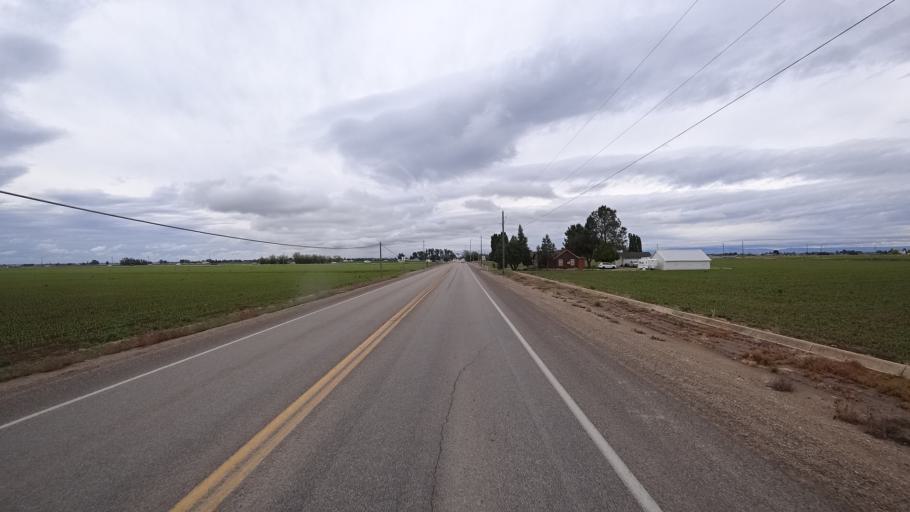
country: US
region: Idaho
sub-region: Ada County
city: Star
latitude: 43.6658
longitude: -116.4934
